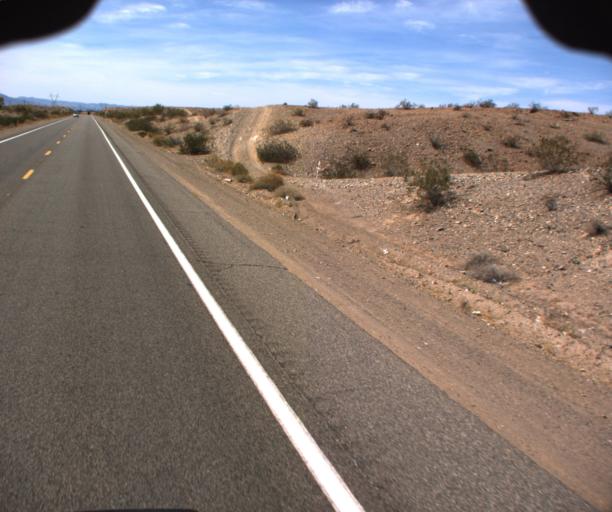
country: US
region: Arizona
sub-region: Mohave County
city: Lake Havasu City
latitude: 34.4420
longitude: -114.2317
